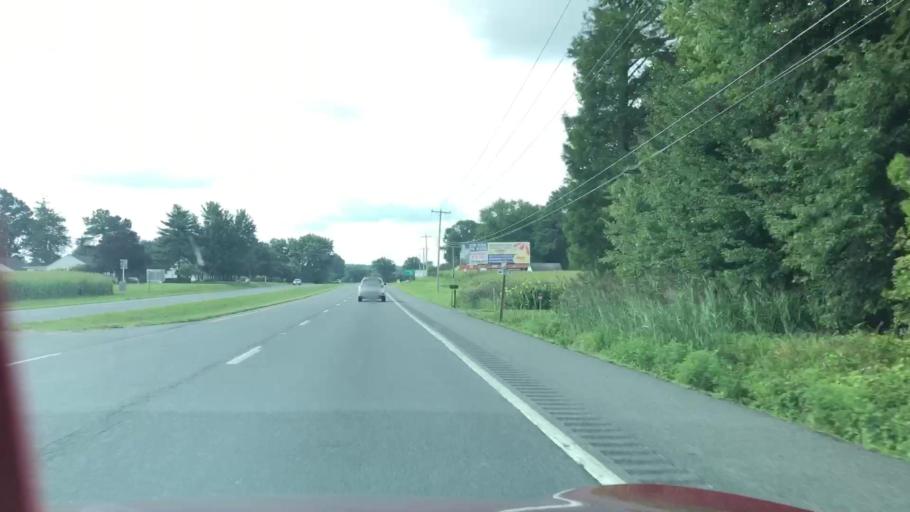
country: US
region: Virginia
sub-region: Accomack County
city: Wattsville
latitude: 37.9621
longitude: -75.5331
